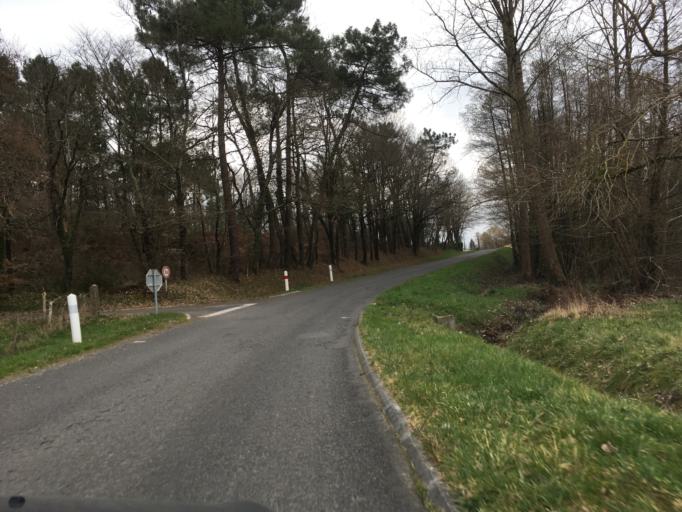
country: FR
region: Poitou-Charentes
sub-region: Departement de la Charente-Maritime
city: Mirambeau
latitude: 45.3297
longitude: -0.5829
